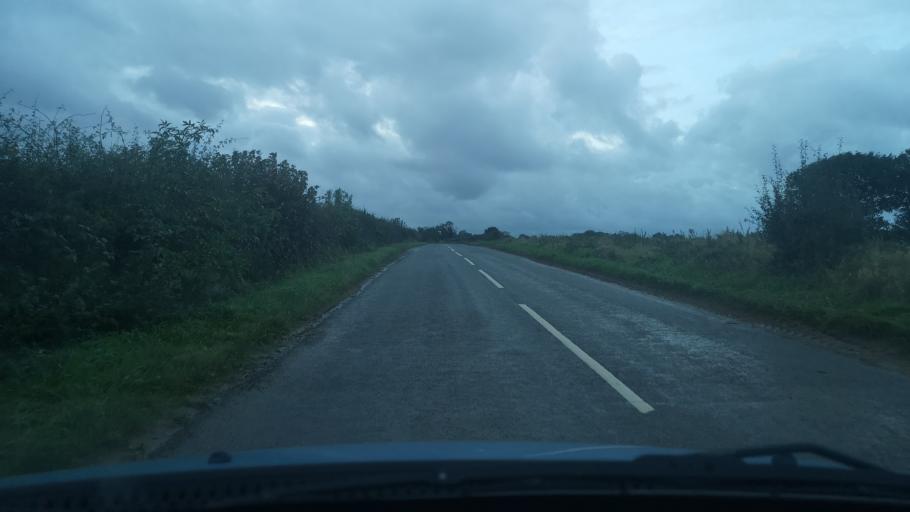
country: GB
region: England
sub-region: Doncaster
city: Norton
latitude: 53.6386
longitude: -1.2105
